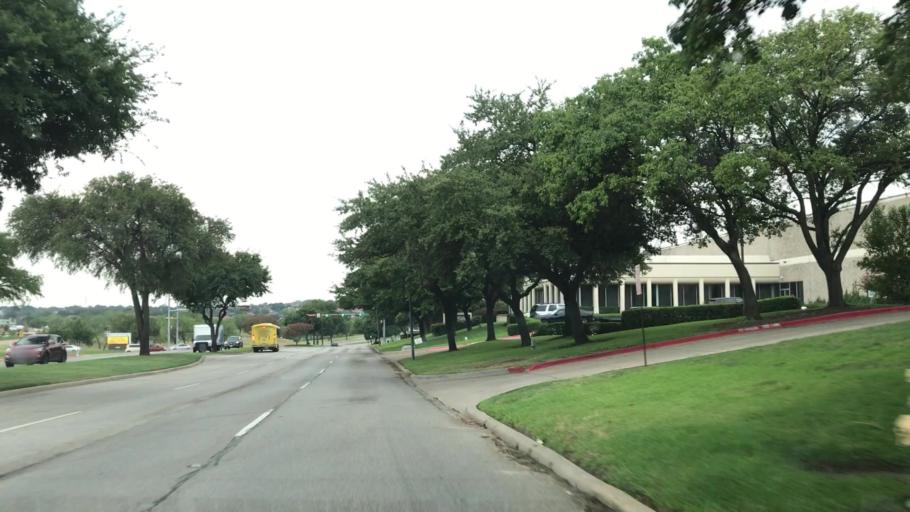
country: US
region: Texas
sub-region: Dallas County
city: Irving
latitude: 32.8731
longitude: -96.9710
